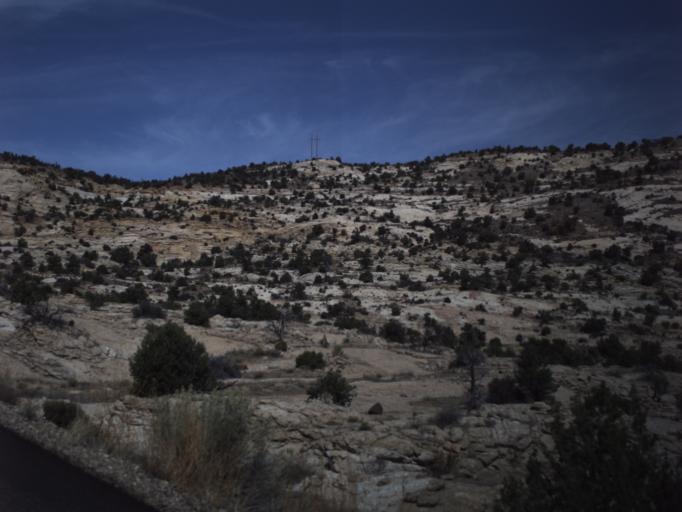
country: US
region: Utah
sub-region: Wayne County
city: Loa
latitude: 37.8098
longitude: -111.4042
